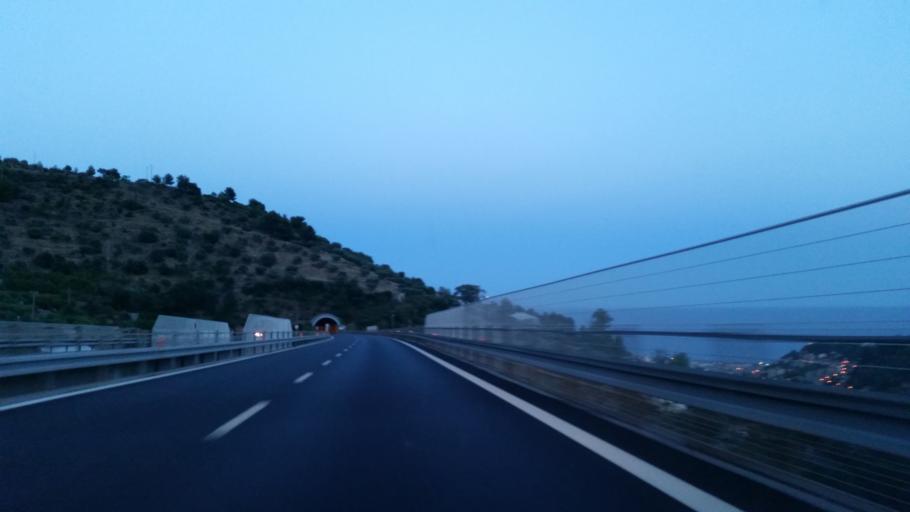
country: IT
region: Liguria
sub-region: Provincia di Imperia
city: San Remo
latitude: 43.8370
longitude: 7.7615
